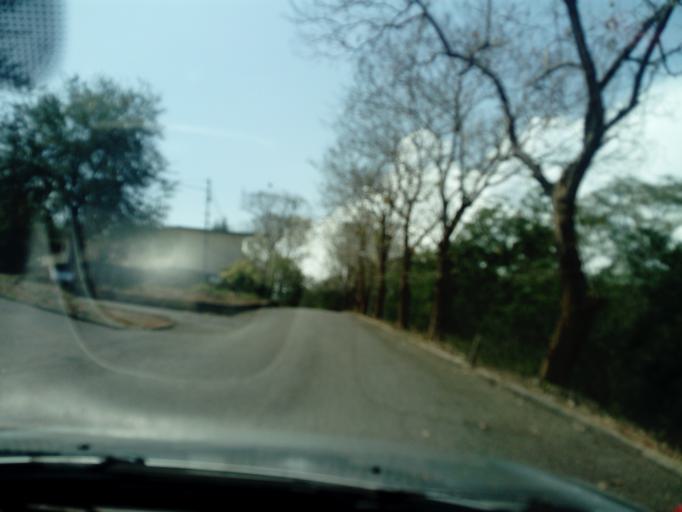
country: GH
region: Central
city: Cape Coast
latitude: 5.1071
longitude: -1.2826
